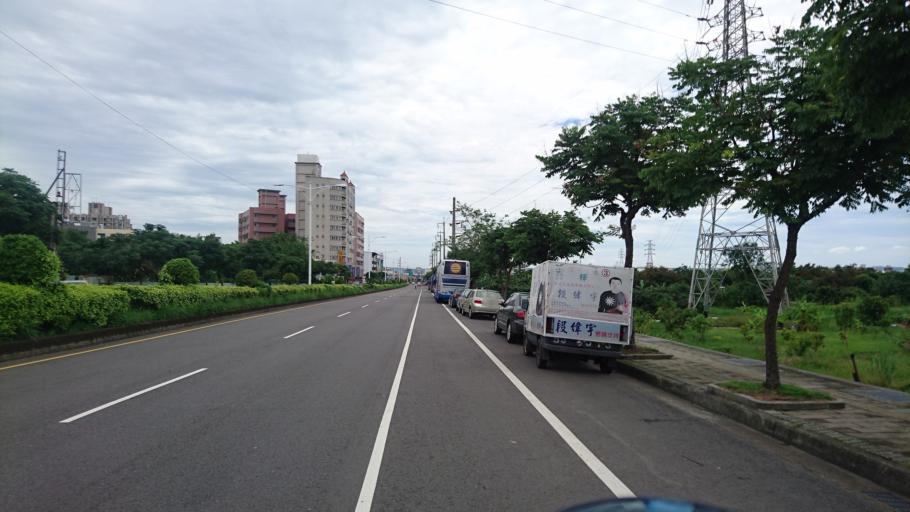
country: TW
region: Taiwan
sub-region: Taichung City
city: Taichung
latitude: 24.0727
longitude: 120.6989
